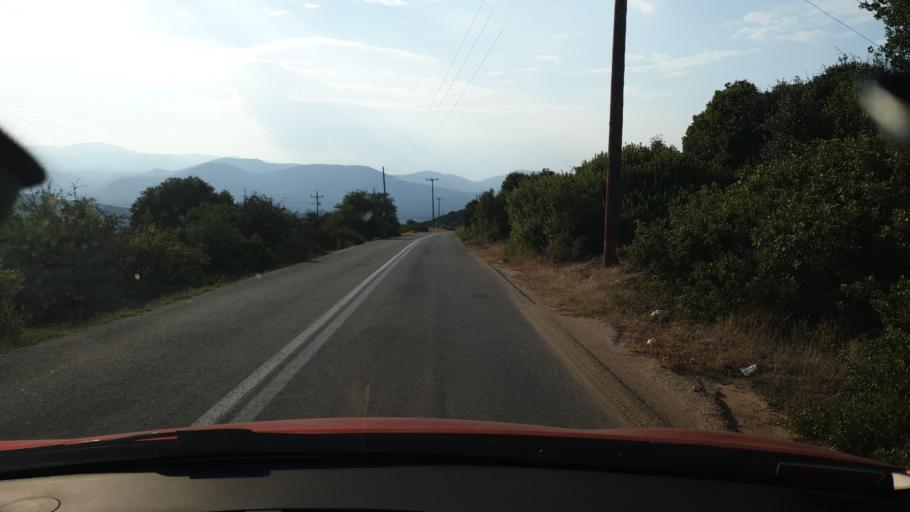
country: GR
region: Thessaly
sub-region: Nomos Magnisias
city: Pteleos
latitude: 39.0596
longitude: 22.9339
